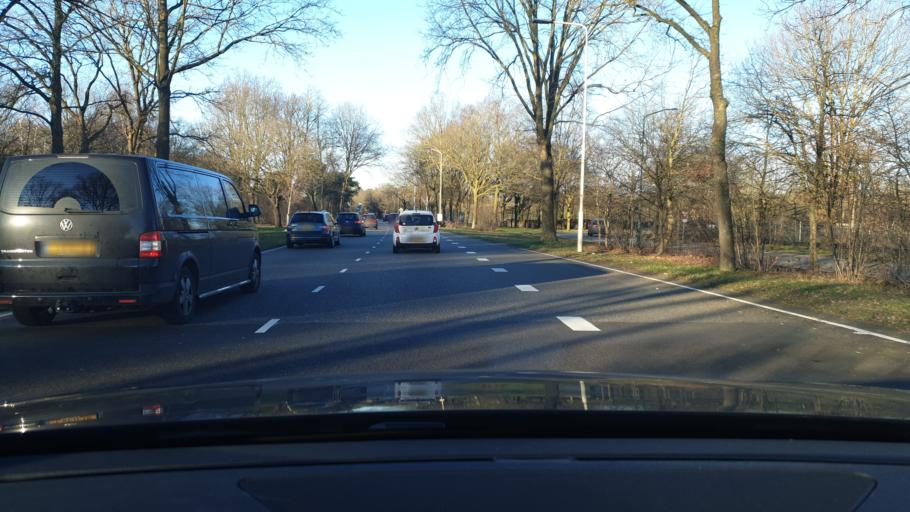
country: NL
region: North Brabant
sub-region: Gemeente Bernheze
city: Heesch
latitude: 51.7391
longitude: 5.5094
